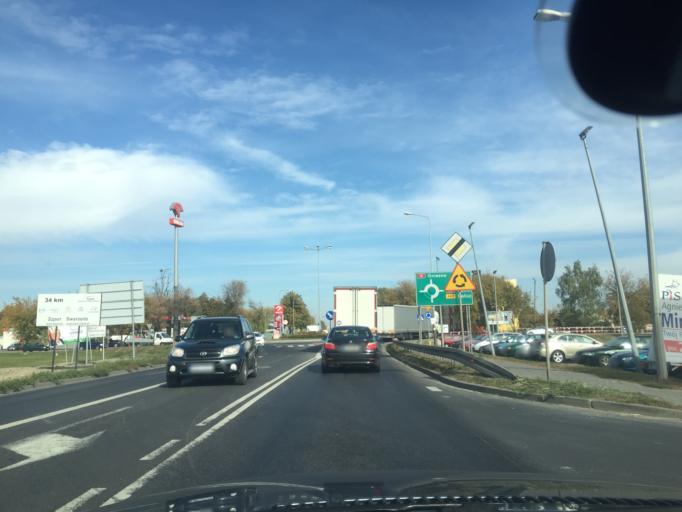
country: PL
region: Greater Poland Voivodeship
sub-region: Powiat wrzesinski
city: Wrzesnia
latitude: 52.3130
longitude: 17.5541
